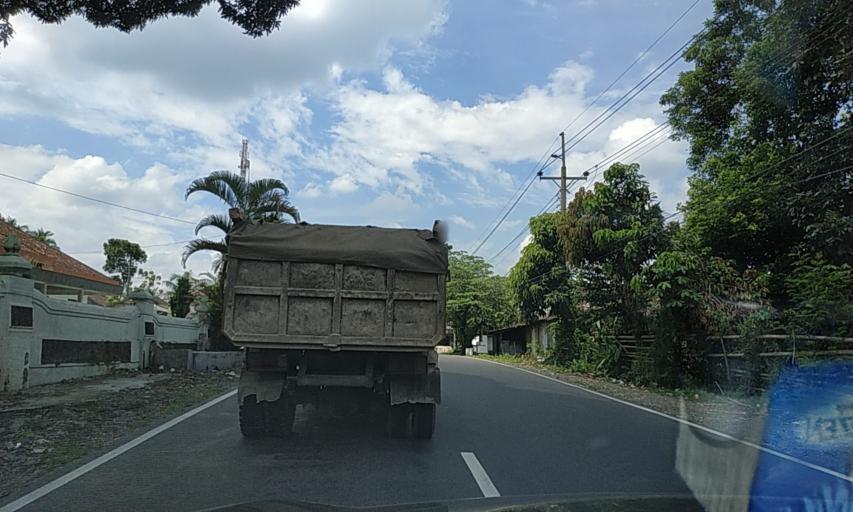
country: ID
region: Central Java
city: Jogonalan
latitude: -7.6644
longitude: 110.4617
